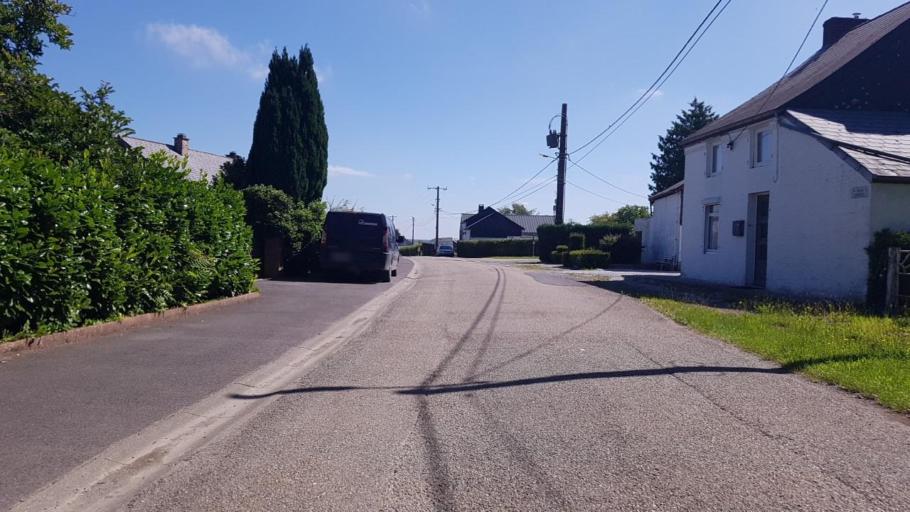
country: BE
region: Wallonia
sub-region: Province du Hainaut
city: Momignies
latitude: 50.0386
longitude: 4.2003
